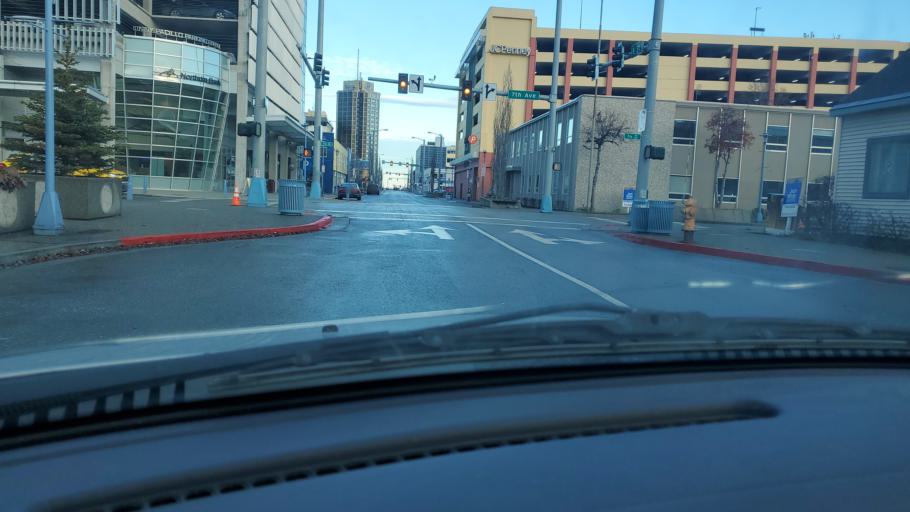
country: US
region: Alaska
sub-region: Anchorage Municipality
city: Anchorage
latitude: 61.2153
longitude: -149.8915
